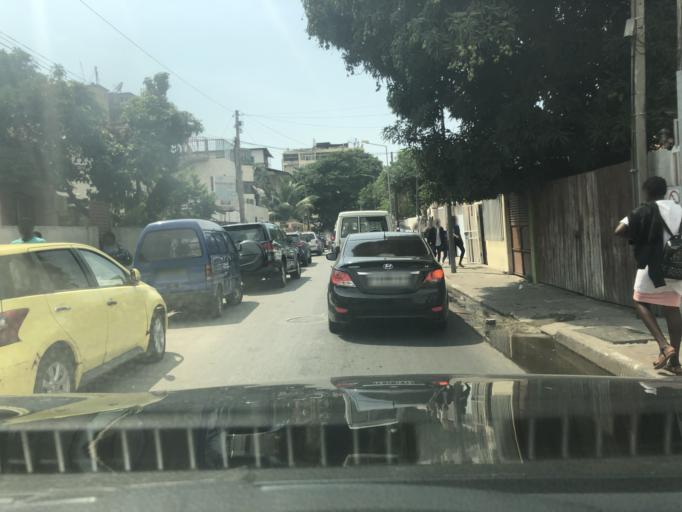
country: AO
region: Luanda
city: Luanda
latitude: -8.8235
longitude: 13.2505
